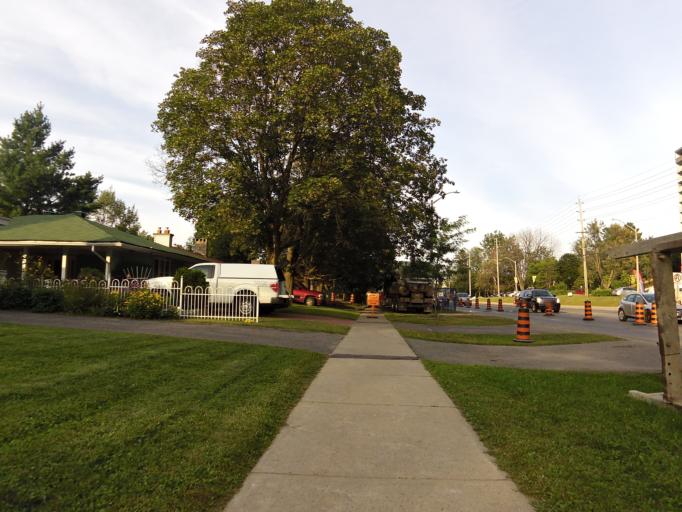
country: CA
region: Ontario
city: Bells Corners
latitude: 45.3440
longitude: -75.7811
